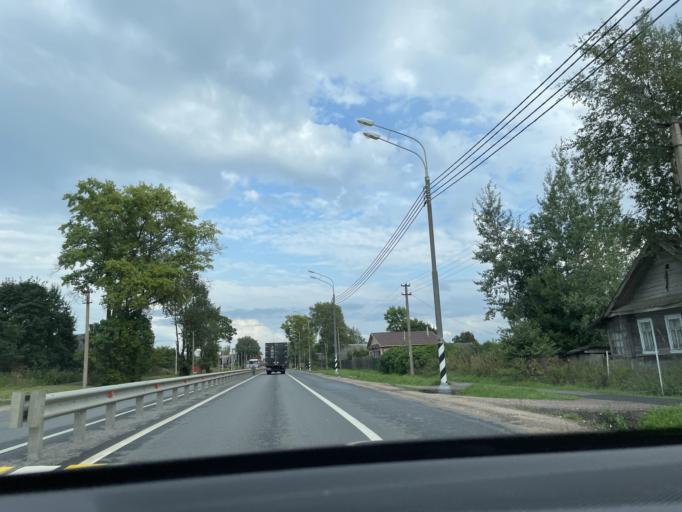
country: RU
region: Tverskaya
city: Kuzhenkino
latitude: 57.7254
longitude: 34.0740
